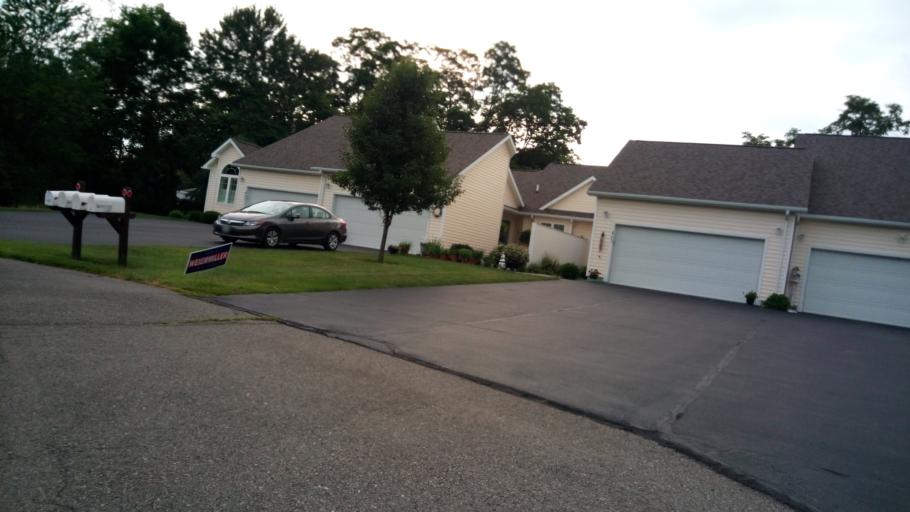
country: US
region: New York
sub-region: Chemung County
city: West Elmira
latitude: 42.0846
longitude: -76.8378
